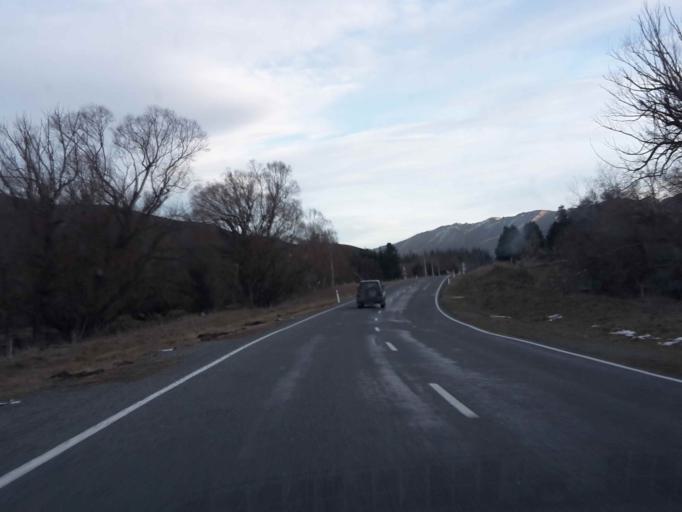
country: NZ
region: Canterbury
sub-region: Timaru District
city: Pleasant Point
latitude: -44.0744
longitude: 170.6666
